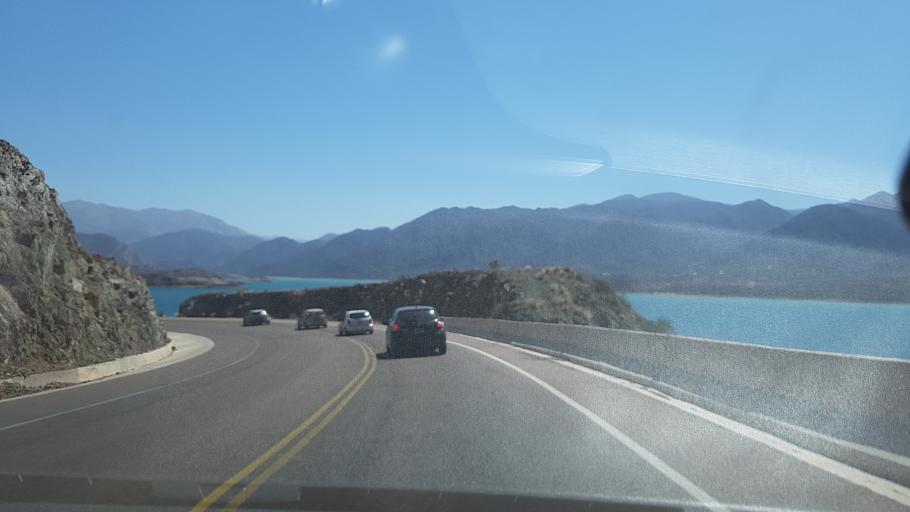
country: AR
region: Mendoza
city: Lujan de Cuyo
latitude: -32.9924
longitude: -69.1537
